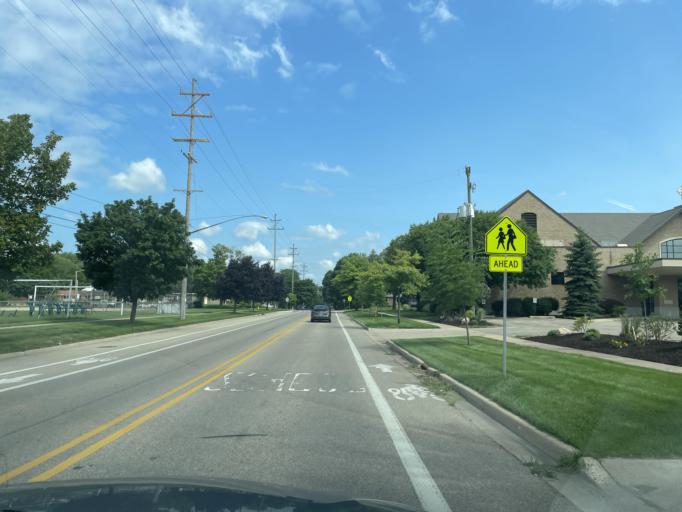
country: US
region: Michigan
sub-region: Kent County
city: East Grand Rapids
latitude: 42.9297
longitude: -85.6241
